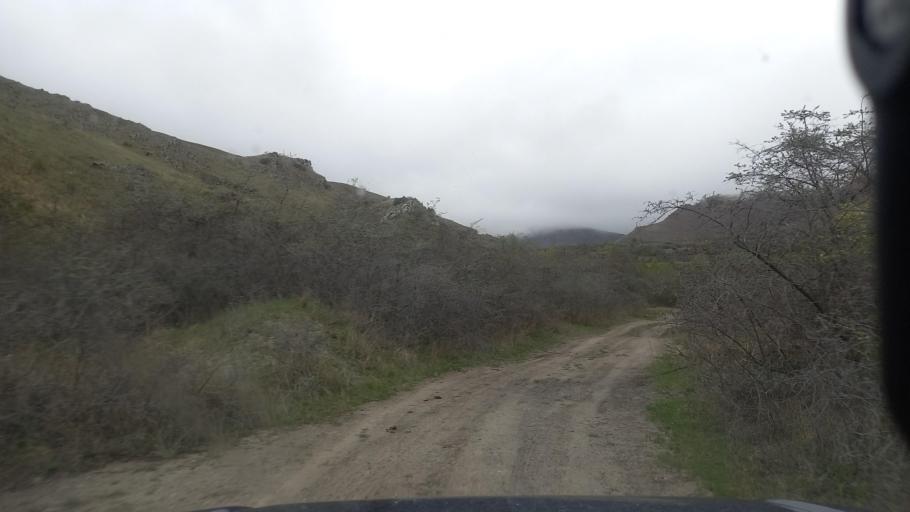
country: RU
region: Kabardino-Balkariya
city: Bylym
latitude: 43.4551
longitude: 43.0003
